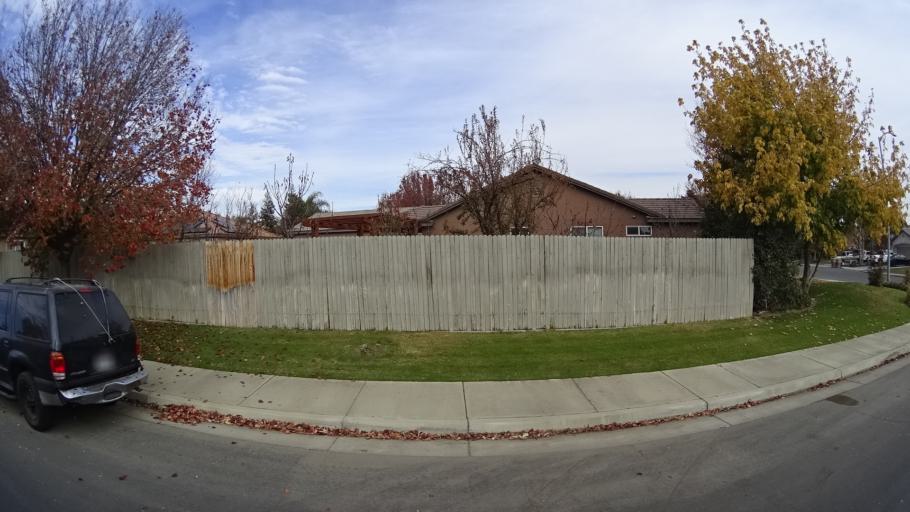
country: US
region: California
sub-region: Kern County
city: Rosedale
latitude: 35.3908
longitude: -119.1356
